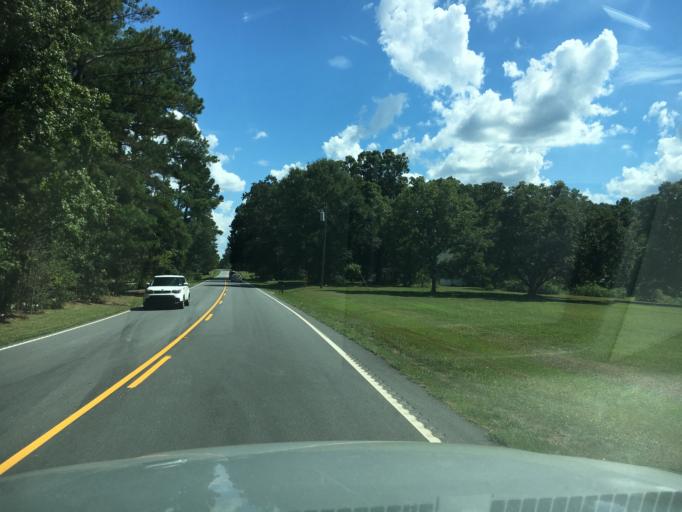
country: US
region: South Carolina
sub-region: Greenwood County
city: Ware Shoals
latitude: 34.5141
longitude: -82.1858
